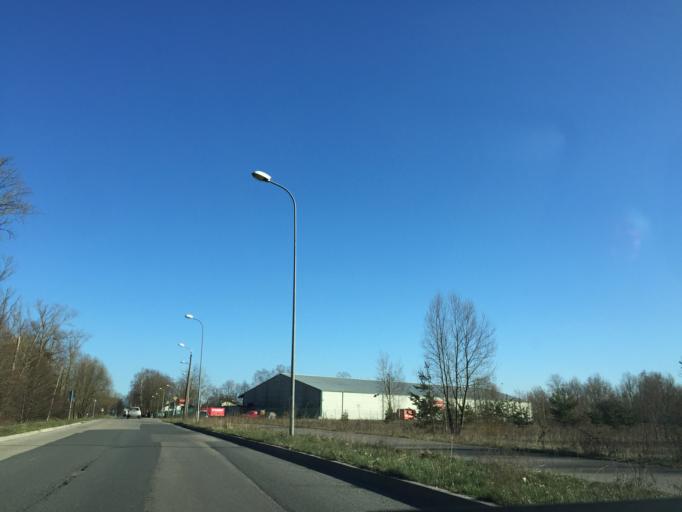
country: LV
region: Marupe
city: Marupe
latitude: 56.9331
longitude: 24.0119
